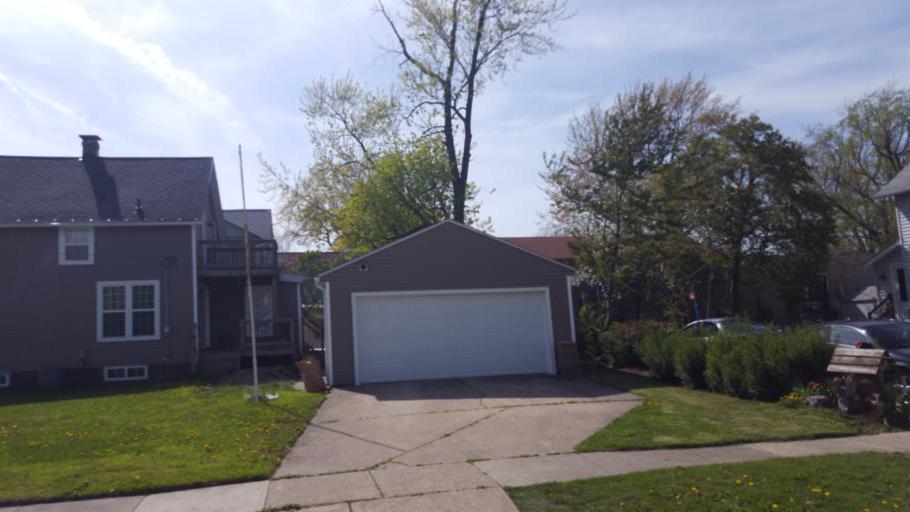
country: US
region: Ohio
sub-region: Lake County
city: Fairport Harbor
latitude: 41.7525
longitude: -81.2756
